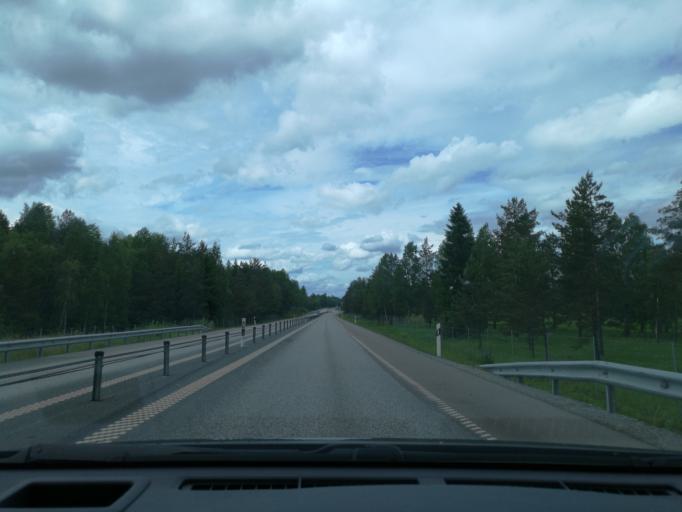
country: SE
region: Vaestmanland
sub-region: Surahammars Kommun
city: Surahammar
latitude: 59.7193
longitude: 16.2388
